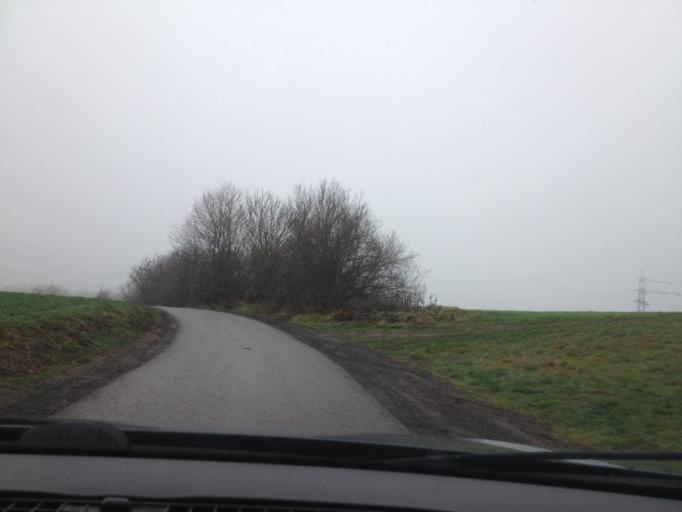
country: DE
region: Saarland
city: Marpingen
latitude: 49.4682
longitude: 7.0859
